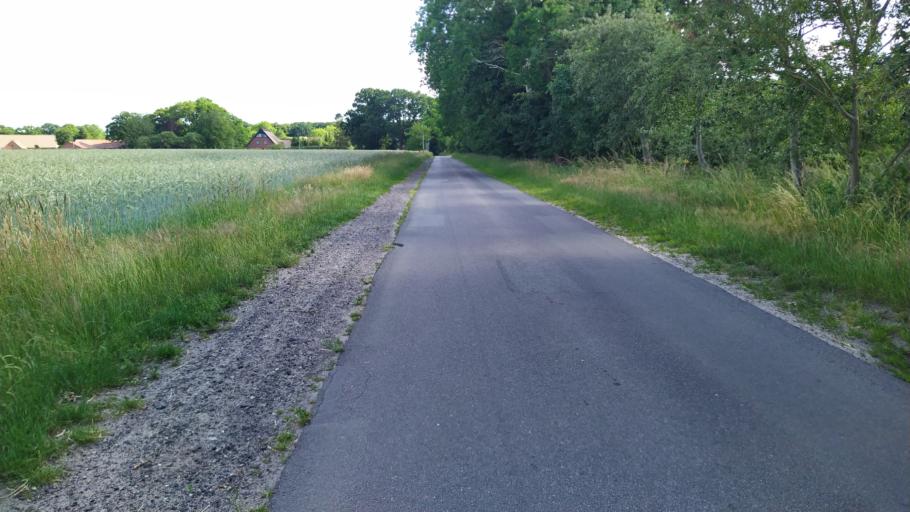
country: DE
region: Lower Saxony
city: Lintig
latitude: 53.6312
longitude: 8.8962
